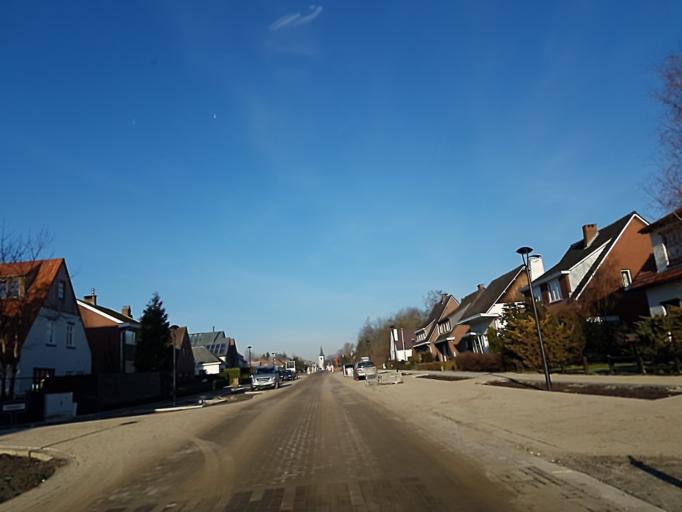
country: BE
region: Flanders
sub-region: Provincie Antwerpen
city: Hove
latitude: 51.1478
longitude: 4.4737
